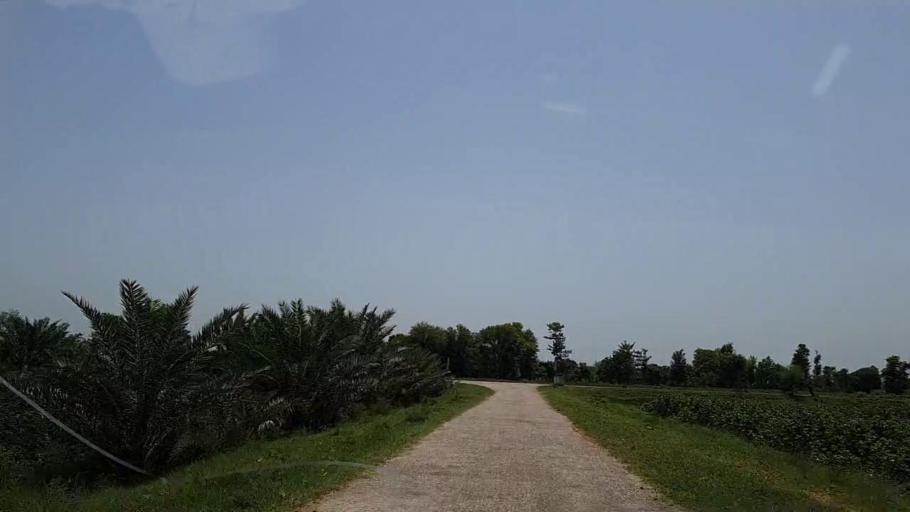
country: PK
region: Sindh
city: Tharu Shah
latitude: 26.9194
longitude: 68.0458
